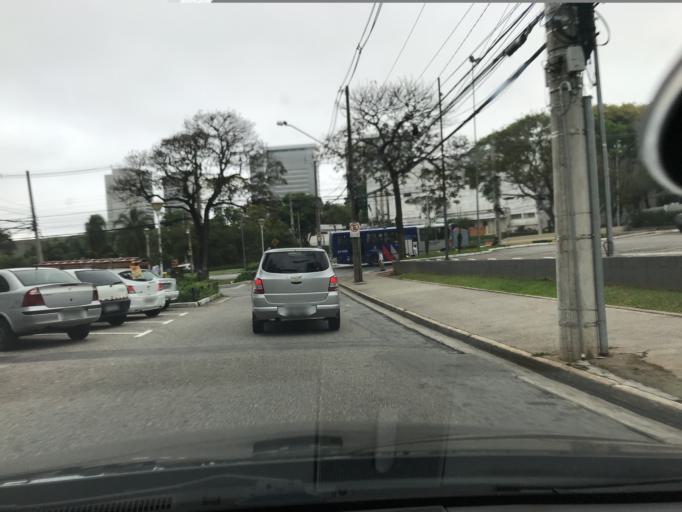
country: BR
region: Sao Paulo
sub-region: Carapicuiba
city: Carapicuiba
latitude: -23.4981
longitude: -46.8471
